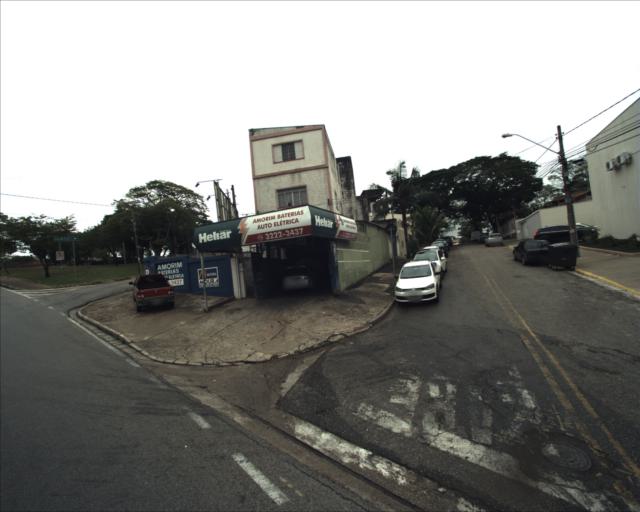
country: BR
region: Sao Paulo
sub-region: Sorocaba
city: Sorocaba
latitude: -23.5179
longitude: -47.4715
